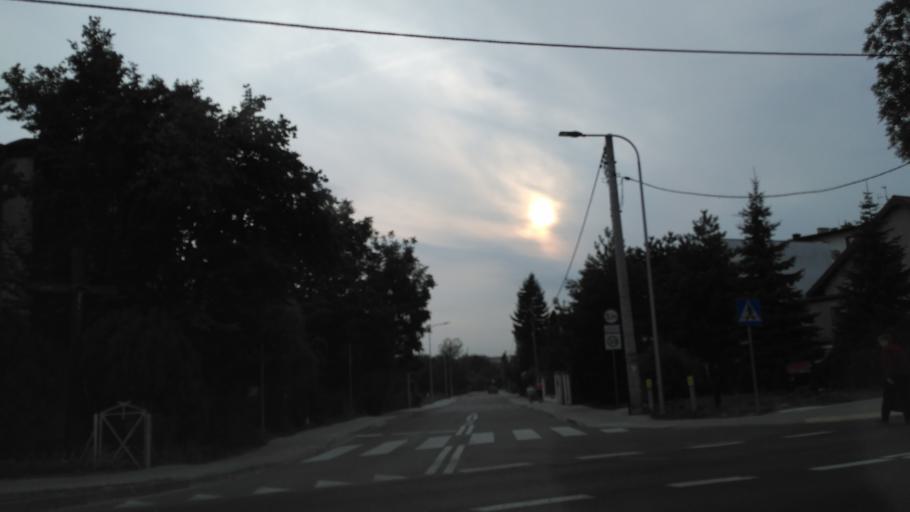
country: PL
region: Lublin Voivodeship
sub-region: Powiat lubelski
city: Lublin
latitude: 51.2244
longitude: 22.5873
